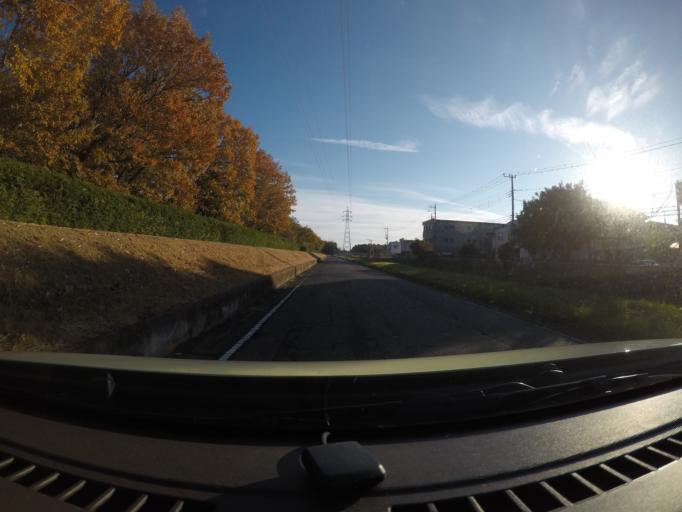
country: JP
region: Ibaraki
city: Tsukuba
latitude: 36.1248
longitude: 140.0891
